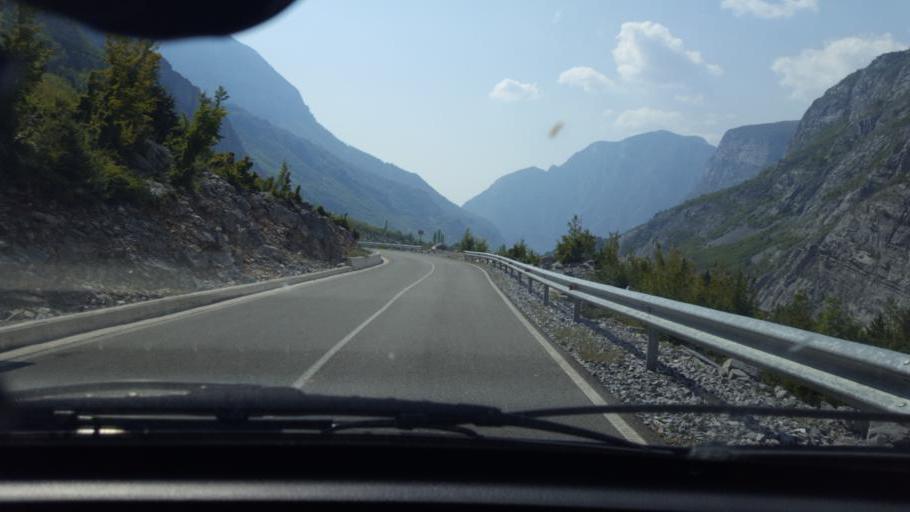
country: AL
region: Shkoder
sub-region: Rrethi i Malesia e Madhe
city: Kastrat
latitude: 42.5187
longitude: 19.6264
